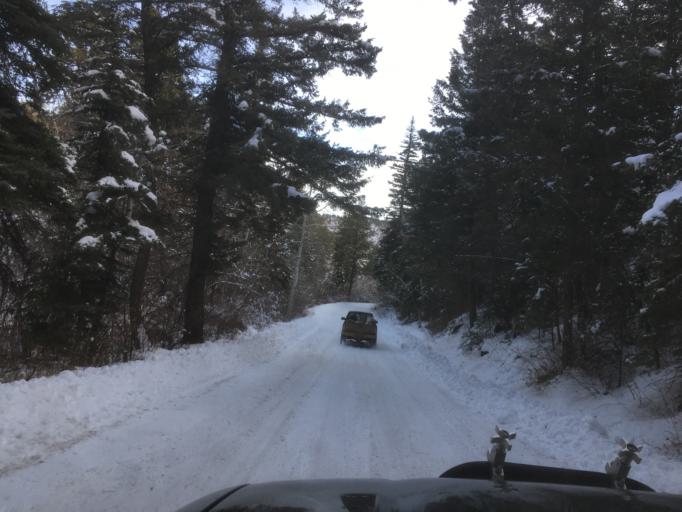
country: US
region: Wyoming
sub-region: Albany County
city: Laramie
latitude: 40.9185
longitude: -105.5115
